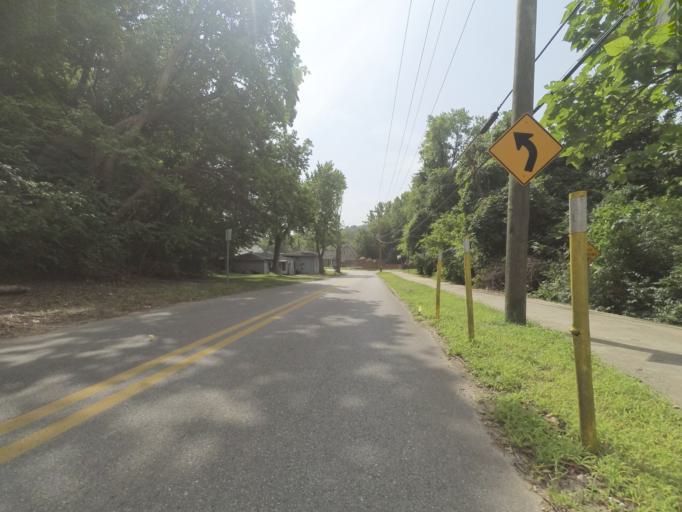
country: US
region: West Virginia
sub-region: Cabell County
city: Huntington
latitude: 38.4028
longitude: -82.4780
